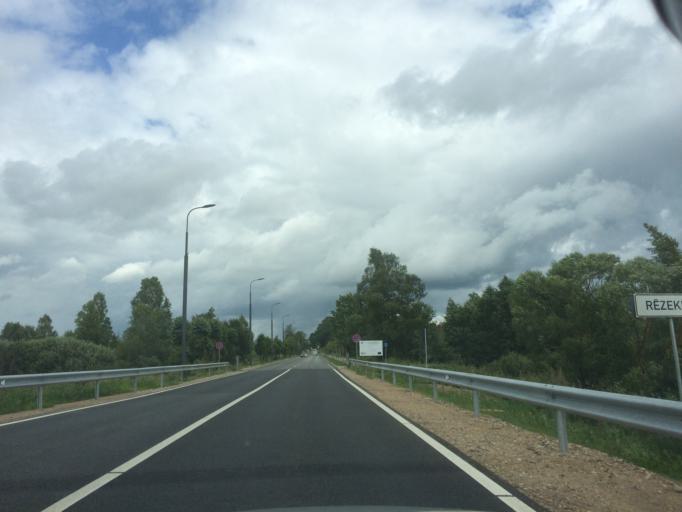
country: LV
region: Rezekne
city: Rezekne
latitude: 56.4910
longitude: 27.3153
